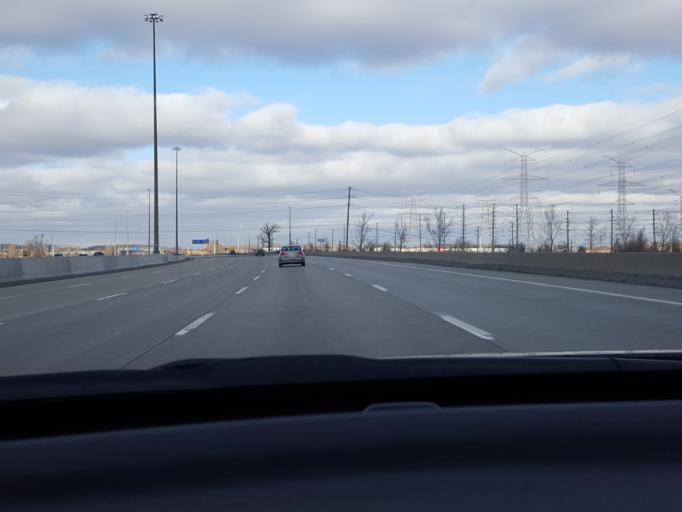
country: CA
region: Ontario
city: Concord
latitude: 43.8037
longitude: -79.4809
